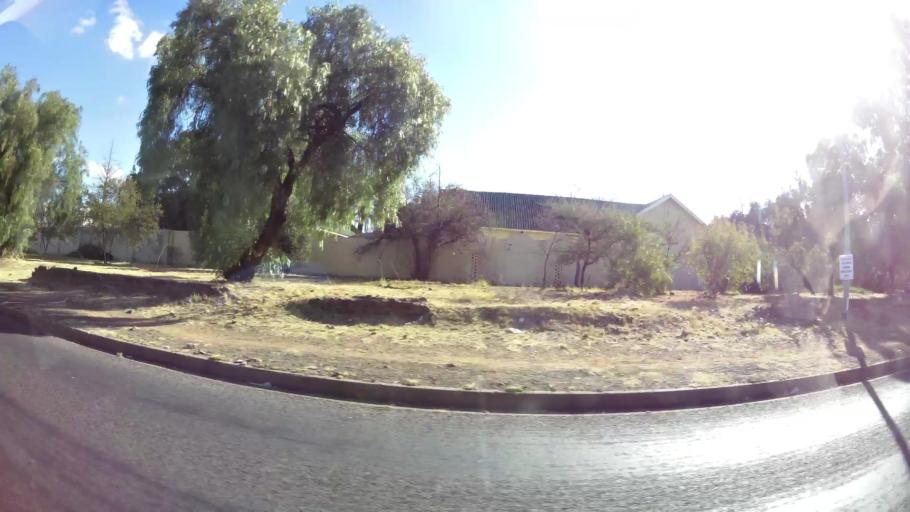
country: ZA
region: Northern Cape
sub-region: Frances Baard District Municipality
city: Kimberley
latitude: -28.7598
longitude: 24.7673
